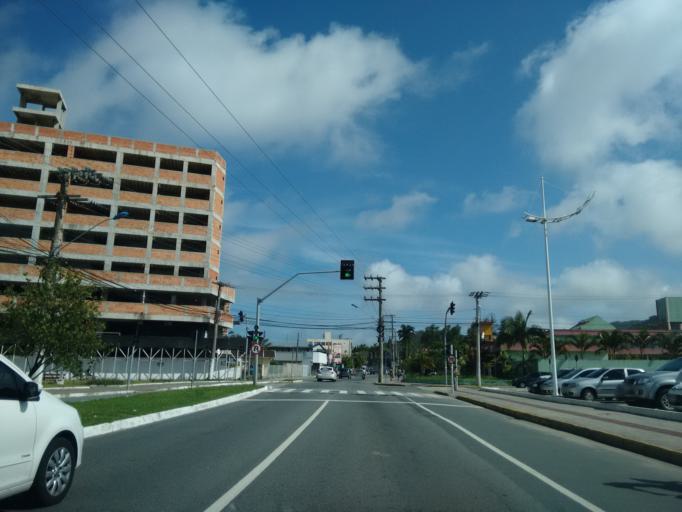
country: BR
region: Santa Catarina
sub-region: Itajai
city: Itajai
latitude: -26.9207
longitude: -48.6536
